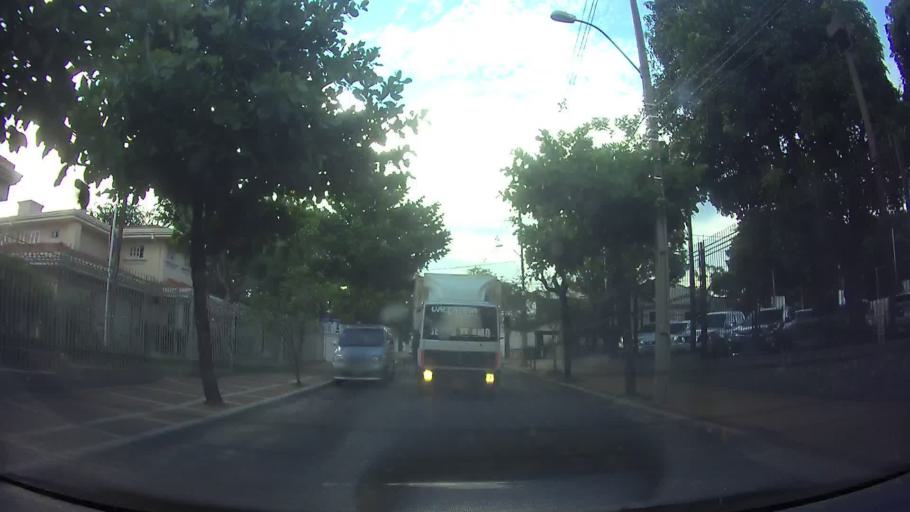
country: PY
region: Asuncion
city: Asuncion
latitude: -25.2873
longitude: -57.6026
